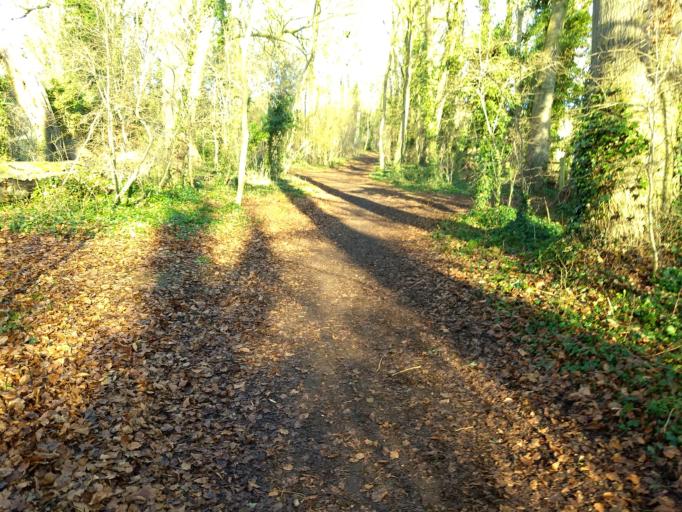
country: GB
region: England
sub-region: Buckinghamshire
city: Buckingham
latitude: 52.0038
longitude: -0.9817
